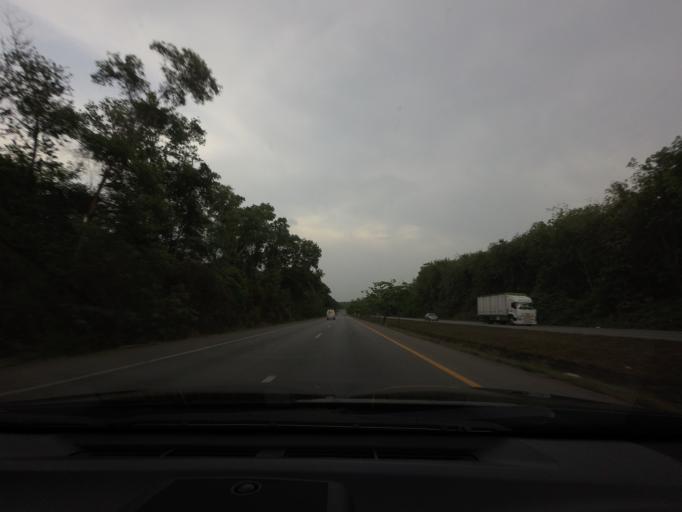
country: TH
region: Surat Thani
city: Chaiya
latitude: 9.4706
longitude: 99.1498
